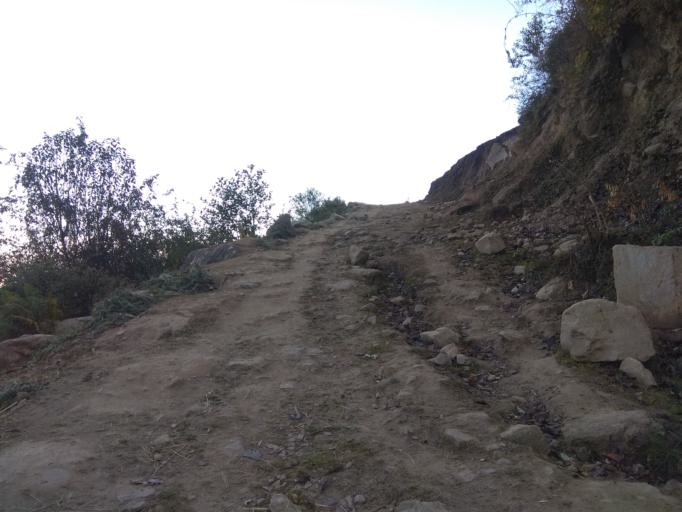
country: NP
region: Mid Western
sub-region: Karnali Zone
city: Jumla
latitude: 29.3176
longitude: 81.7188
